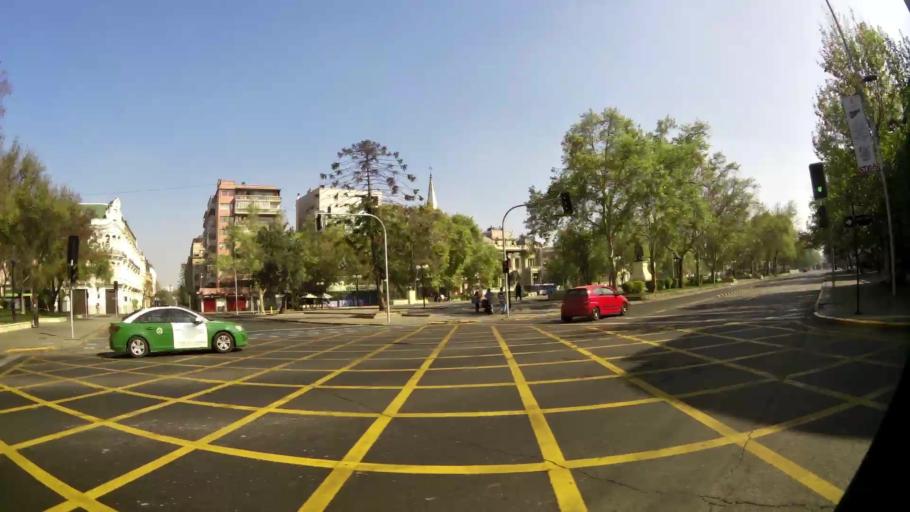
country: CL
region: Santiago Metropolitan
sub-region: Provincia de Santiago
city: Santiago
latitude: -33.4456
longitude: -70.6586
